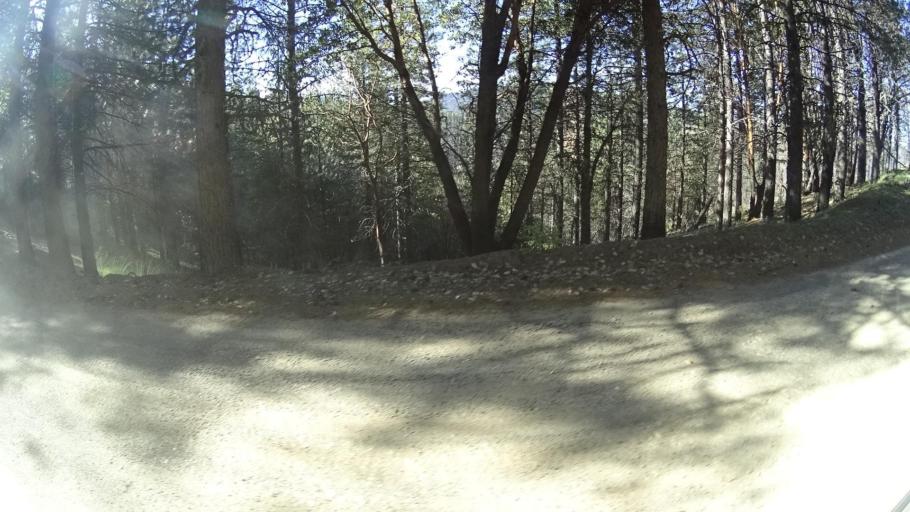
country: US
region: California
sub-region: Lake County
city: Upper Lake
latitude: 39.3499
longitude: -122.9724
